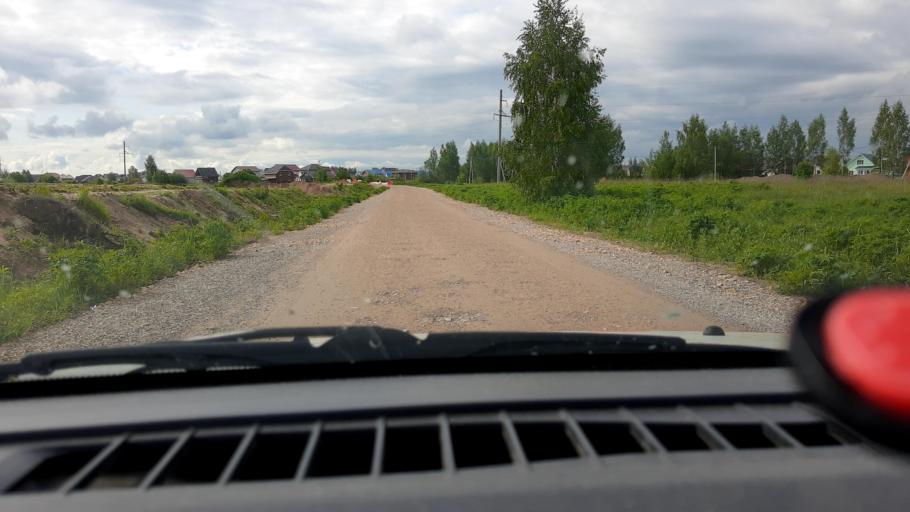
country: RU
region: Nizjnij Novgorod
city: Neklyudovo
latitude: 56.4285
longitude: 43.9625
